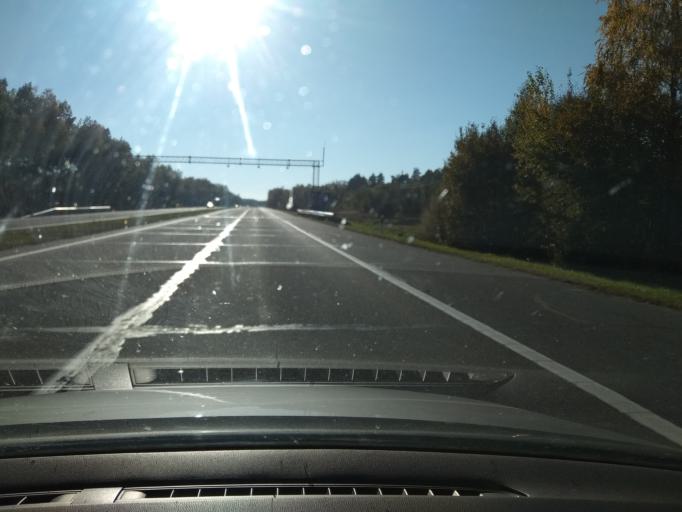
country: BY
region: Brest
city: Ivatsevichy
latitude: 52.6832
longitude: 25.3328
